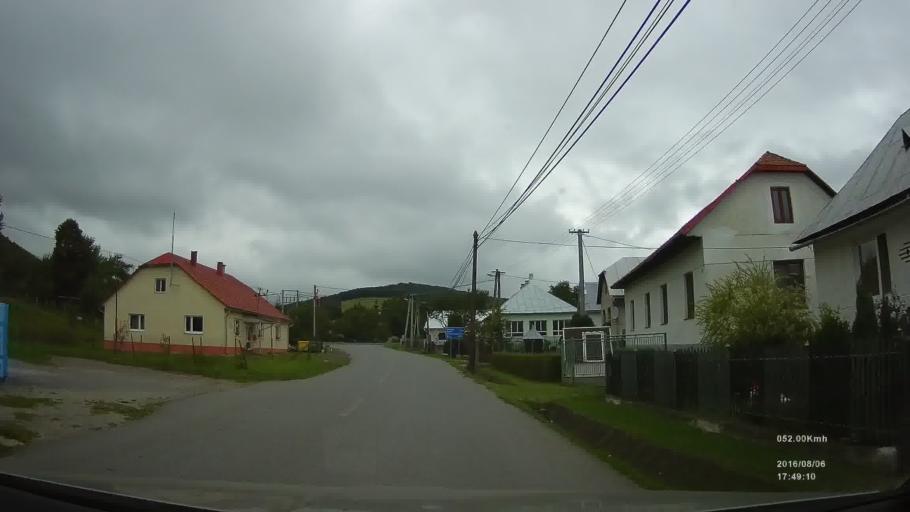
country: SK
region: Presovsky
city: Svidnik
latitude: 49.3819
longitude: 21.5710
